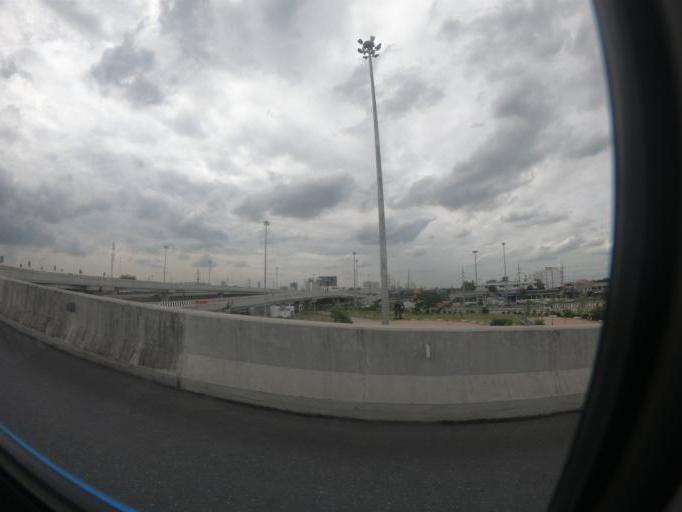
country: TH
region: Bangkok
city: Suan Luang
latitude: 13.7163
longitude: 100.6615
